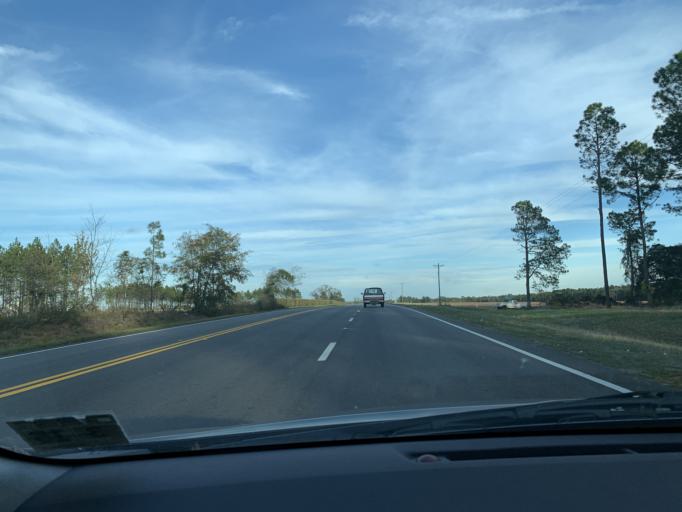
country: US
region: Georgia
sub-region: Irwin County
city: Ocilla
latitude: 31.5942
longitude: -83.1882
